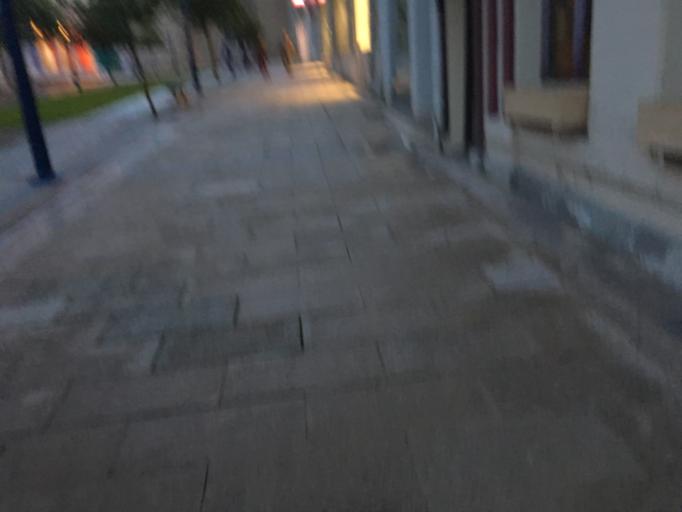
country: FR
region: Lorraine
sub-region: Departement de la Meuse
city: Verdun
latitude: 49.1613
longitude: 5.3855
